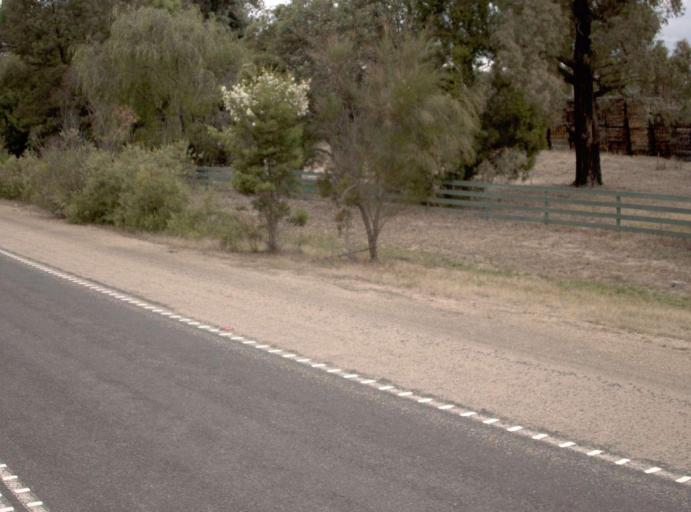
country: AU
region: Victoria
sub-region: East Gippsland
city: Lakes Entrance
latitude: -37.7252
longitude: 148.0876
